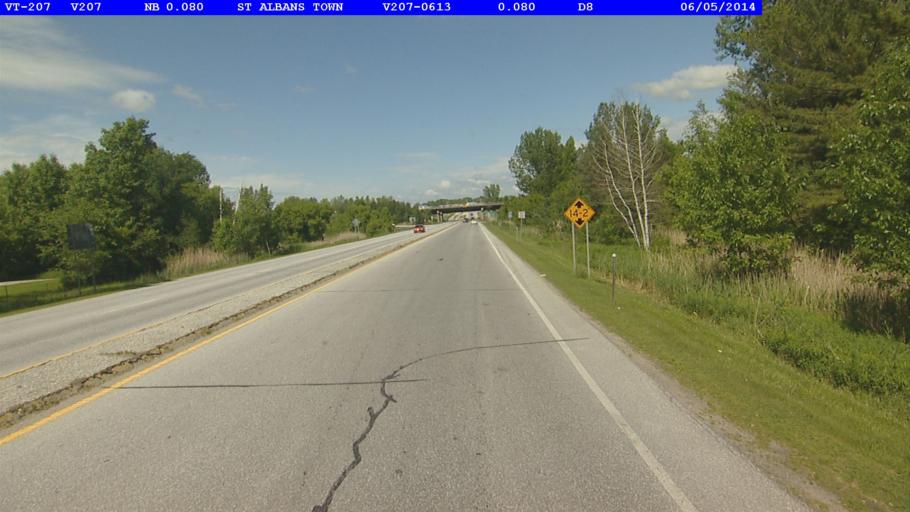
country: US
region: Vermont
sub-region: Franklin County
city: Saint Albans
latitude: 44.8415
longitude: -73.0822
